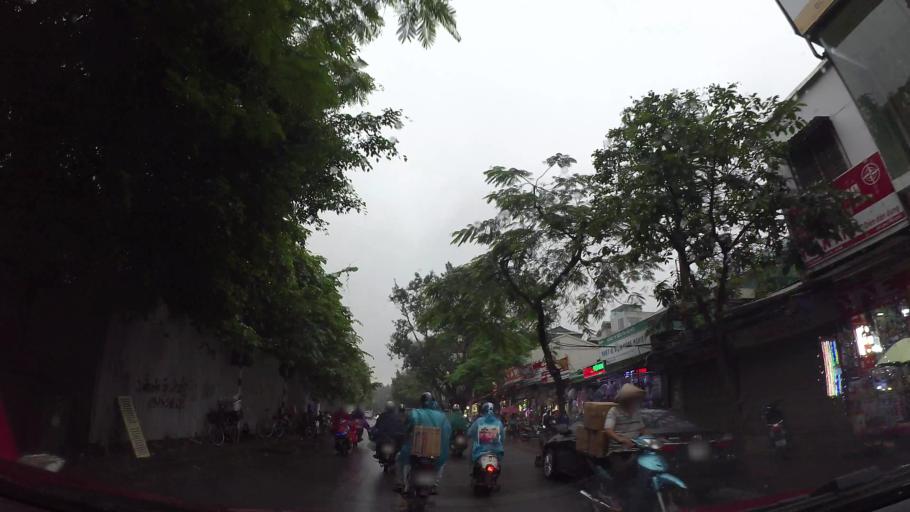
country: VN
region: Ha Noi
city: Hai BaTrung
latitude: 21.0138
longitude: 105.8537
